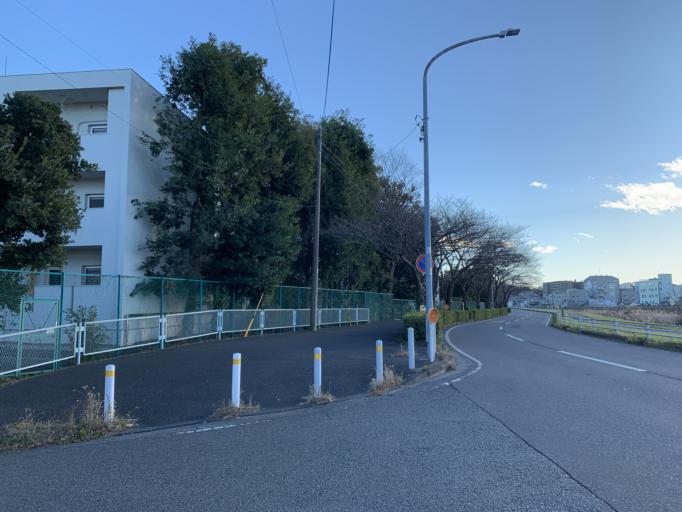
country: JP
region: Tokyo
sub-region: Machida-shi
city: Machida
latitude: 35.5175
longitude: 139.5522
